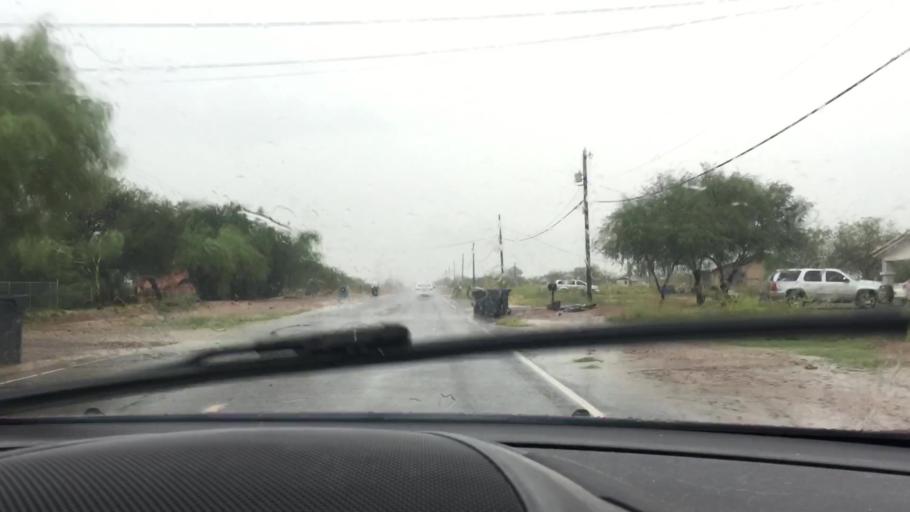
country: US
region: Arizona
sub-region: Maricopa County
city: Scottsdale
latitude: 33.4758
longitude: -111.8827
